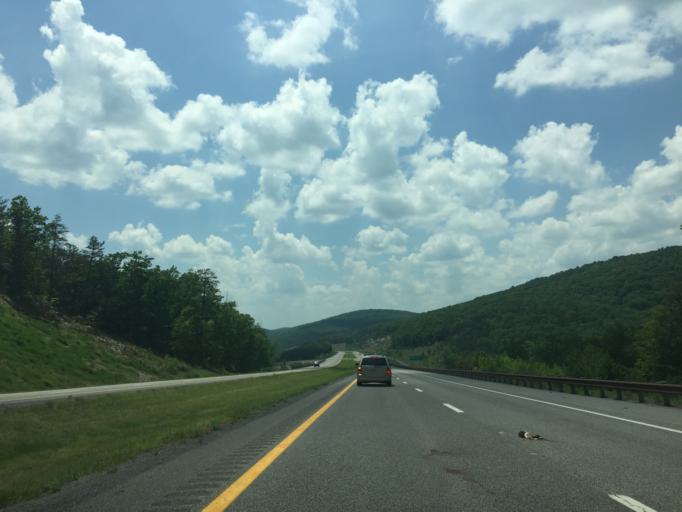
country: US
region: Virginia
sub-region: Shenandoah County
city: Woodstock
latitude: 39.0543
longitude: -78.6945
